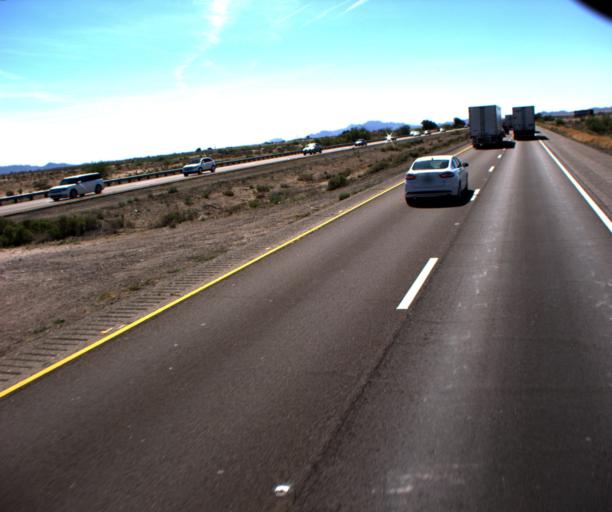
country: US
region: Arizona
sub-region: Pinal County
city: Casa Blanca
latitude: 33.1452
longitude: -111.8633
